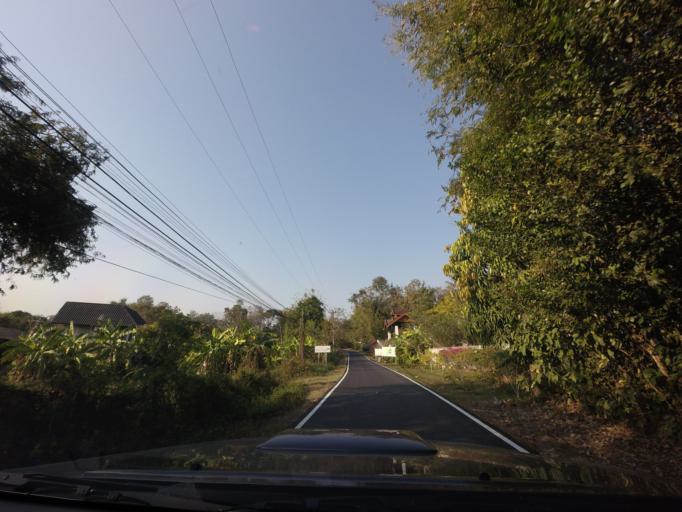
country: TH
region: Chiang Mai
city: Chiang Mai
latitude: 18.9247
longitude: 98.9092
